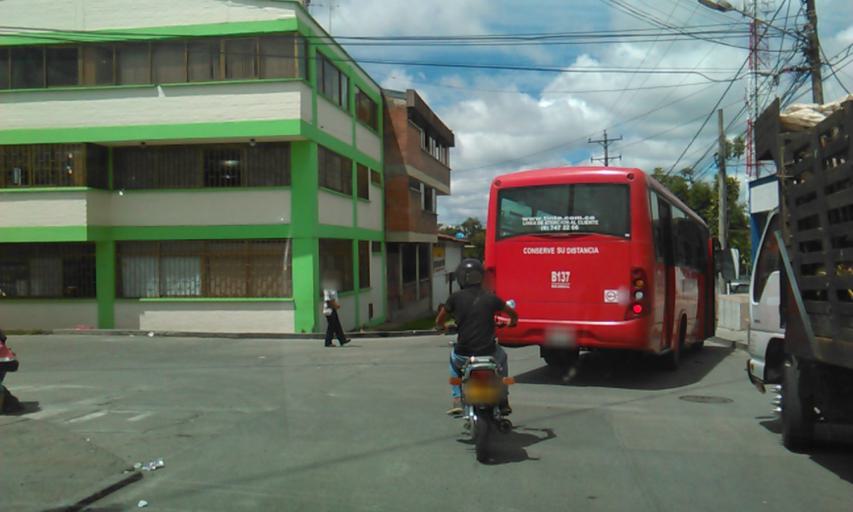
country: CO
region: Quindio
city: Armenia
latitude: 4.5154
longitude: -75.6884
